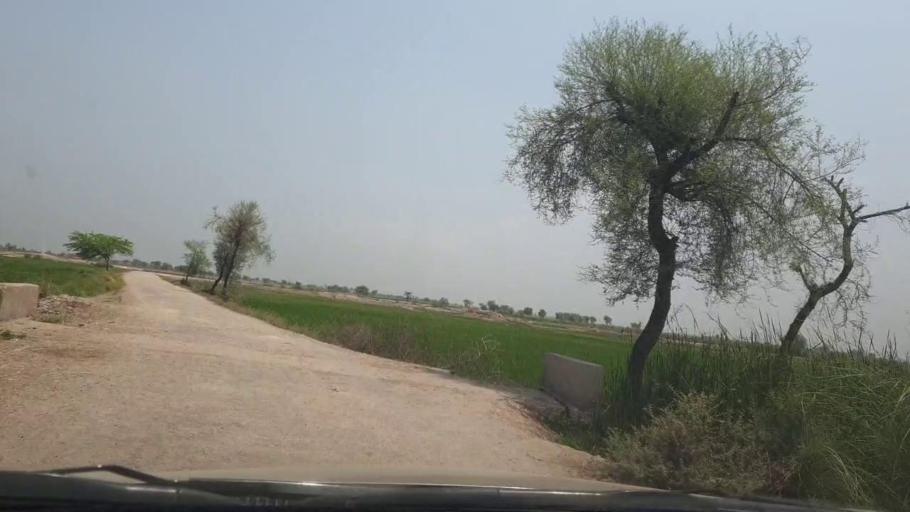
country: PK
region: Sindh
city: Ratodero
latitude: 27.7218
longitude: 68.2855
